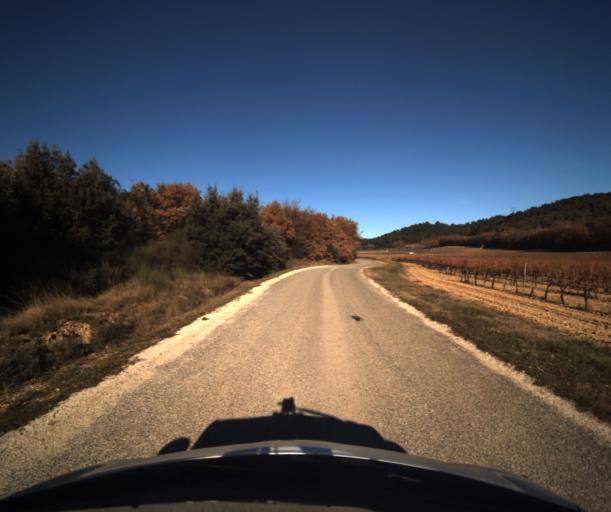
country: FR
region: Provence-Alpes-Cote d'Azur
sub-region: Departement du Vaucluse
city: Ansouis
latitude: 43.7050
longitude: 5.4660
